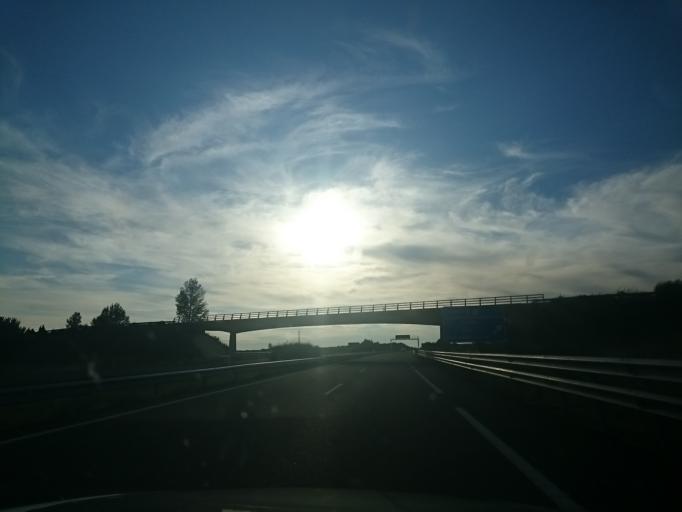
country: ES
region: Castille and Leon
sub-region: Provincia de Leon
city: Sahagun
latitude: 42.3779
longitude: -5.0101
